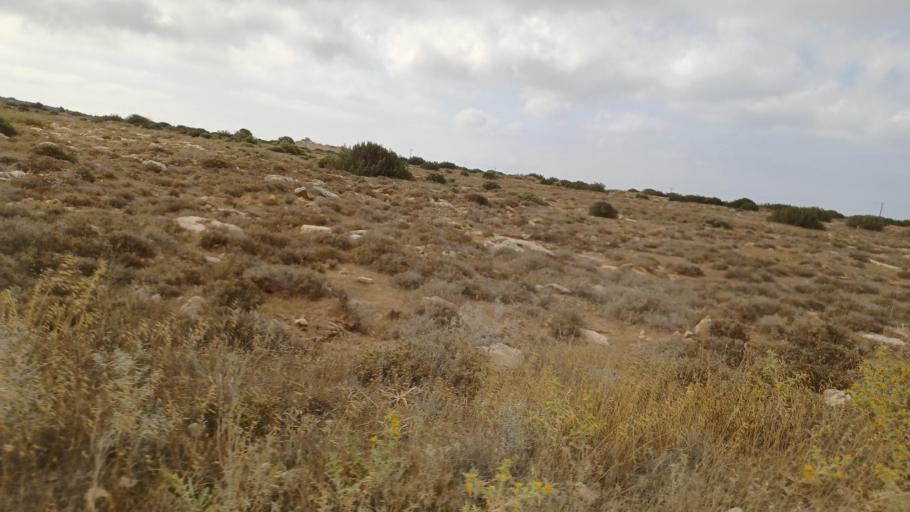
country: CY
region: Ammochostos
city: Ayia Napa
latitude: 34.9990
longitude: 34.0217
